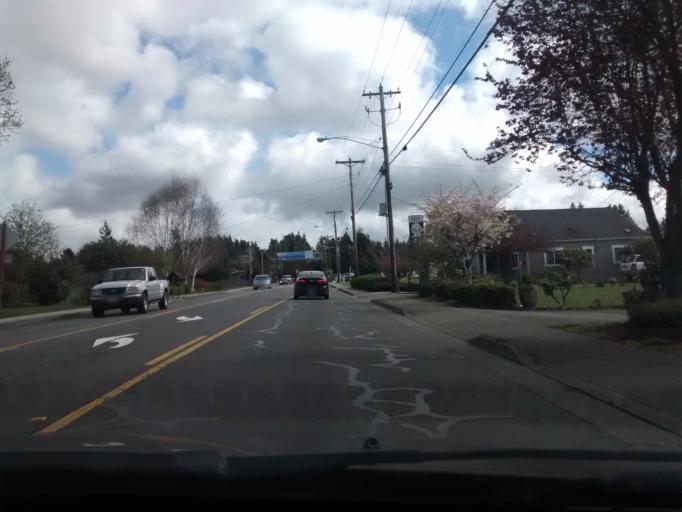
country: US
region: Washington
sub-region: Snohomish County
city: Edmonds
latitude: 47.8178
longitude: -122.3713
